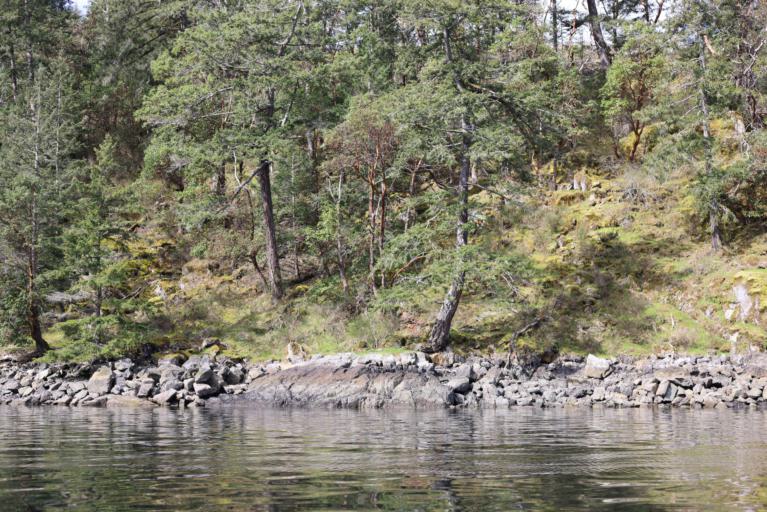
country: CA
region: British Columbia
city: Langford
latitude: 48.5168
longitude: -123.5422
